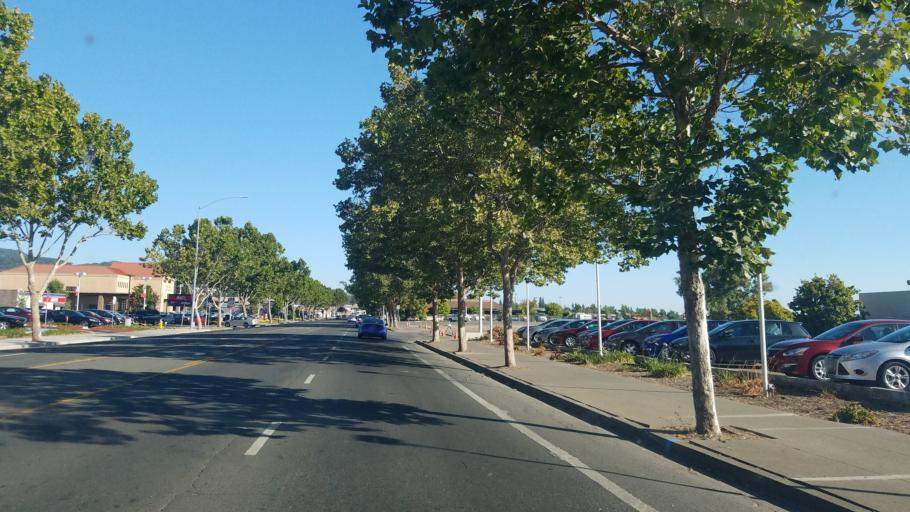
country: US
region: California
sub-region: Napa County
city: Napa
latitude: 38.2919
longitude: -122.2778
